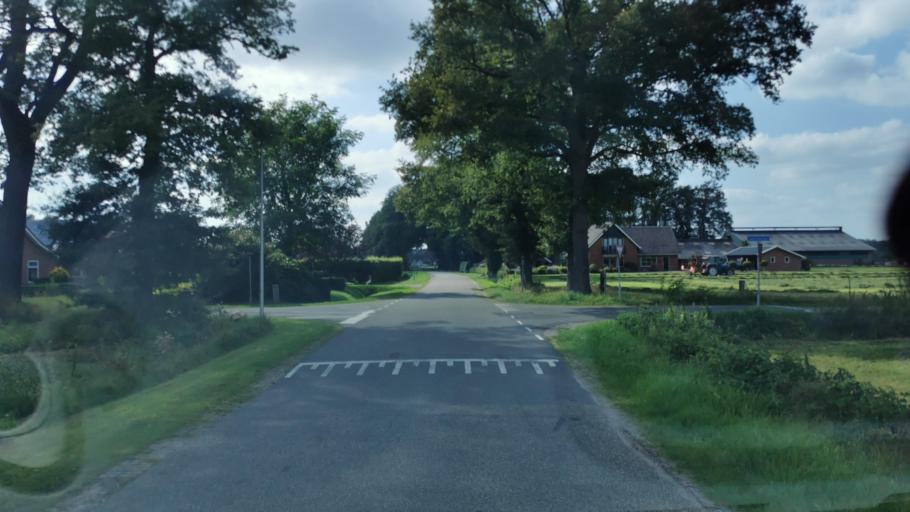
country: NL
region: Overijssel
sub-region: Gemeente Hengelo
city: Hengelo
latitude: 52.3236
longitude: 6.8291
